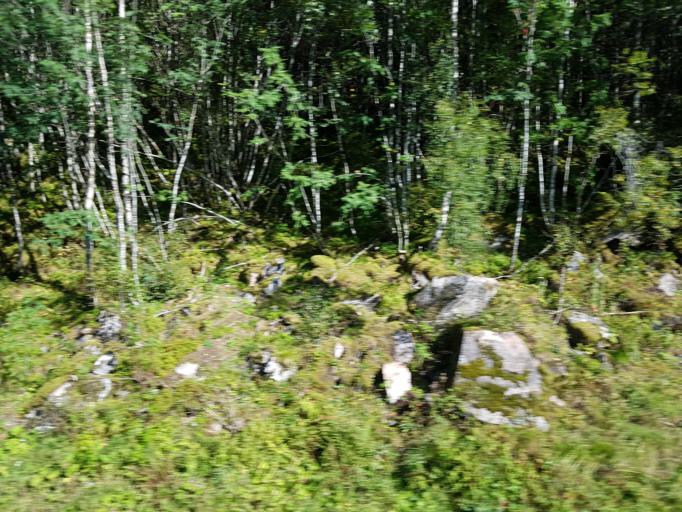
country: NO
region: Sor-Trondelag
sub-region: Afjord
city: A i Afjord
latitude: 63.7466
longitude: 10.2374
